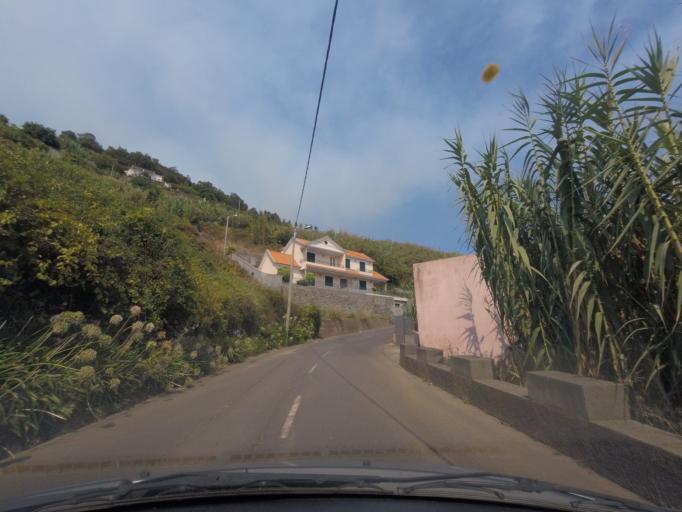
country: PT
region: Madeira
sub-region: Ribeira Brava
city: Campanario
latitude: 32.6888
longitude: -17.0630
